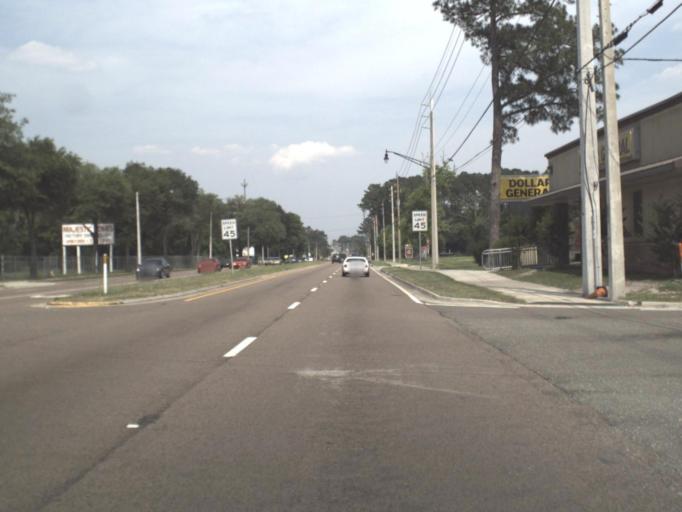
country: US
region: Florida
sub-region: Clay County
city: Bellair-Meadowbrook Terrace
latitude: 30.2476
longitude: -81.8069
